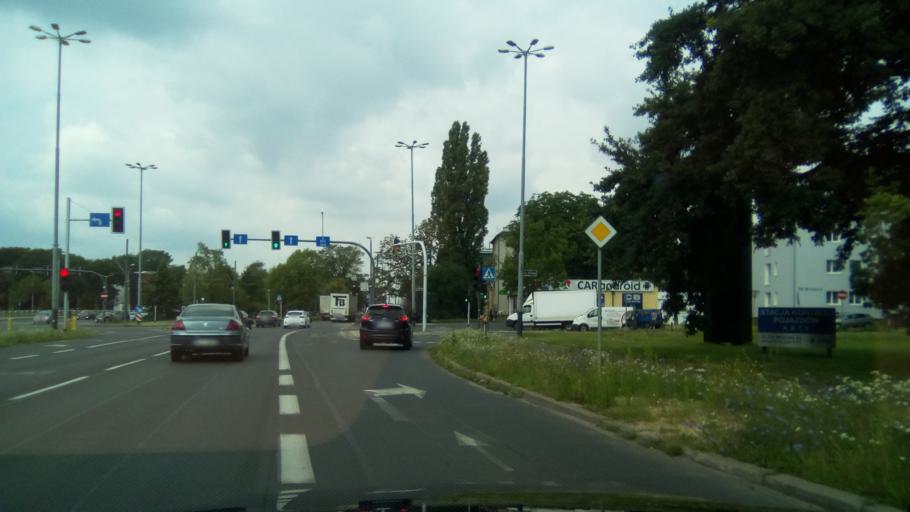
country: PL
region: Greater Poland Voivodeship
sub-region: Poznan
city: Poznan
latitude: 52.4091
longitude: 16.9641
